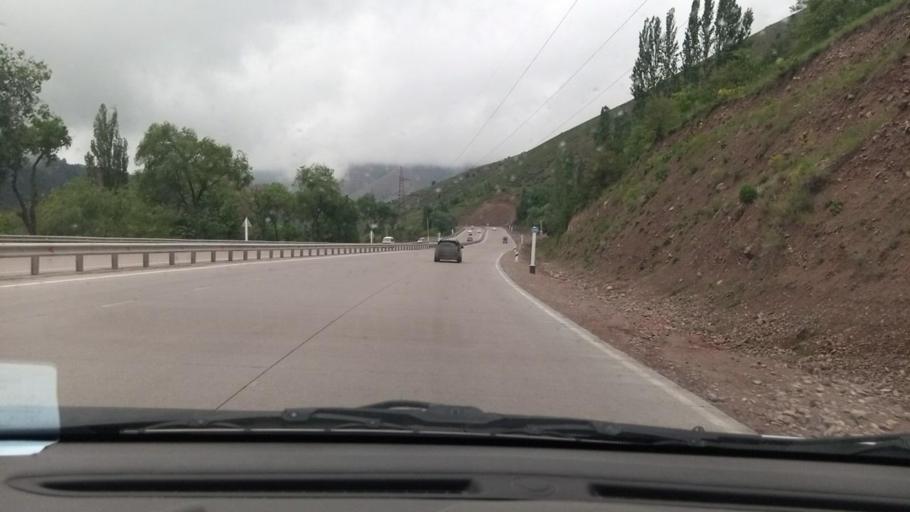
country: UZ
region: Toshkent
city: Angren
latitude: 41.1344
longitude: 70.4621
